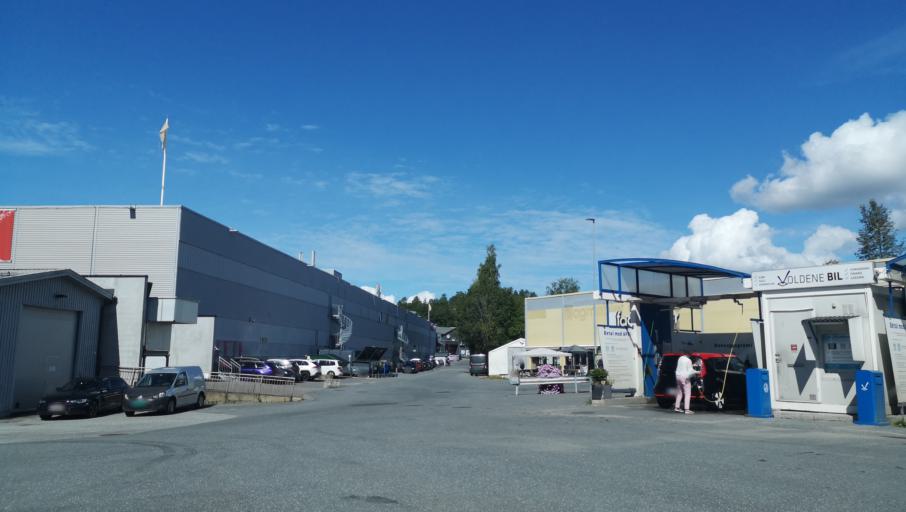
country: NO
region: Akershus
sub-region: Frogn
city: Drobak
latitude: 59.6719
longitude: 10.6598
